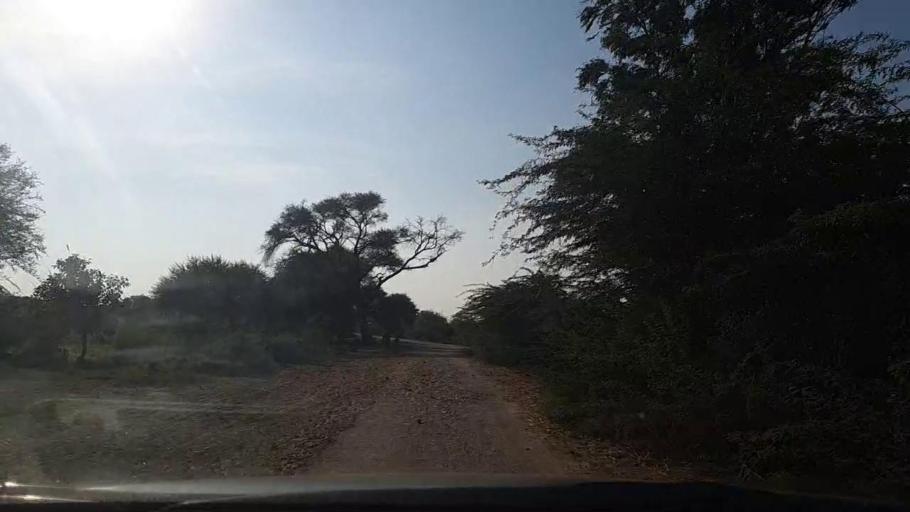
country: PK
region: Sindh
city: Mirpur Sakro
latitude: 24.5344
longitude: 67.6358
